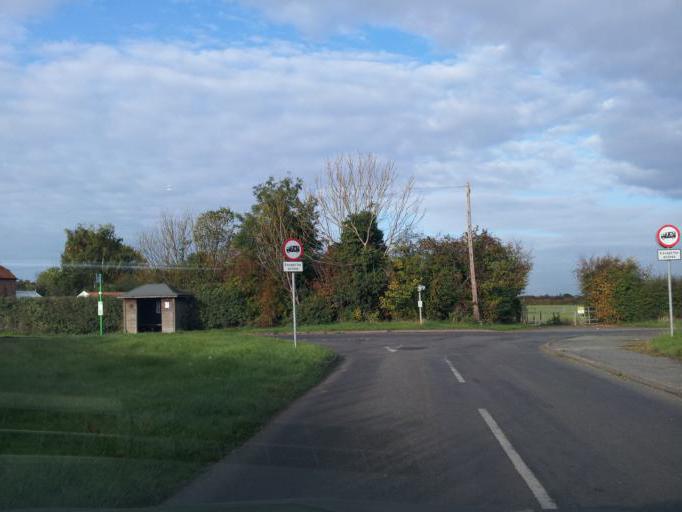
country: GB
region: England
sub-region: Lincolnshire
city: Long Bennington
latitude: 52.9847
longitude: -0.8043
